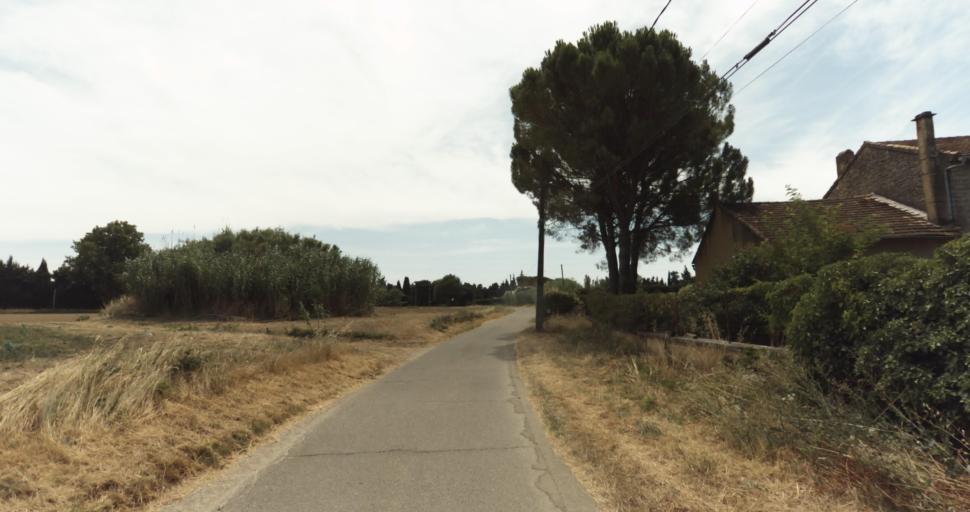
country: FR
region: Provence-Alpes-Cote d'Azur
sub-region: Departement du Vaucluse
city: Monteux
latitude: 44.0499
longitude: 4.9901
